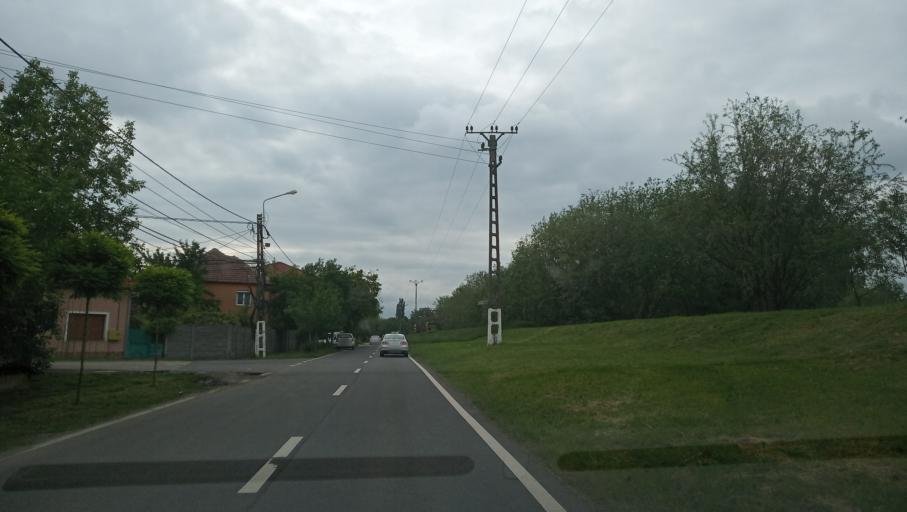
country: RO
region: Timis
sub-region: Comuna Ghiroda
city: Ghiroda
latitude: 45.7538
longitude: 21.2789
